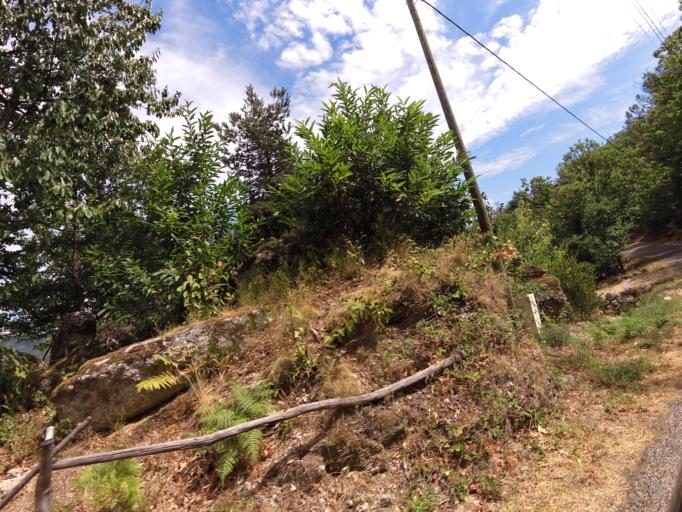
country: FR
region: Languedoc-Roussillon
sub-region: Departement du Gard
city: Le Vigan
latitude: 44.0265
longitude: 3.6216
